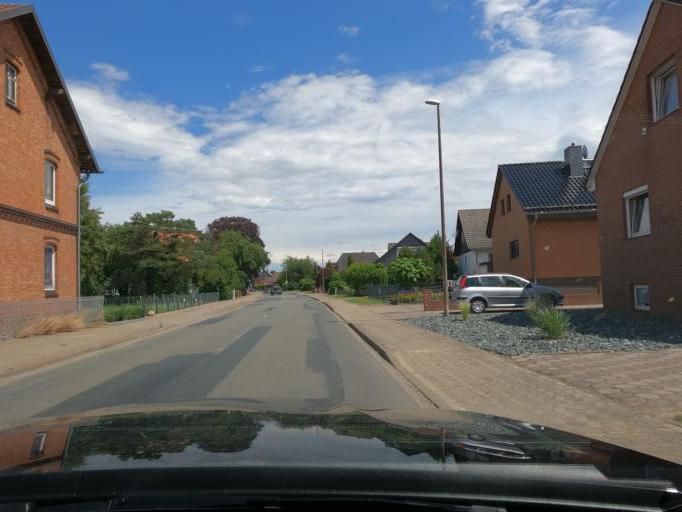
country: DE
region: Lower Saxony
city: Sohlde
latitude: 52.1857
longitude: 10.2023
